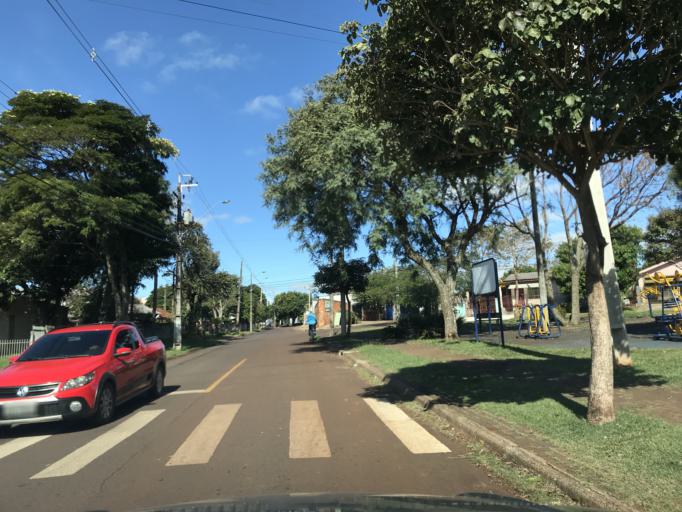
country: BR
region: Parana
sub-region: Cascavel
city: Cascavel
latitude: -24.9383
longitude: -53.4685
